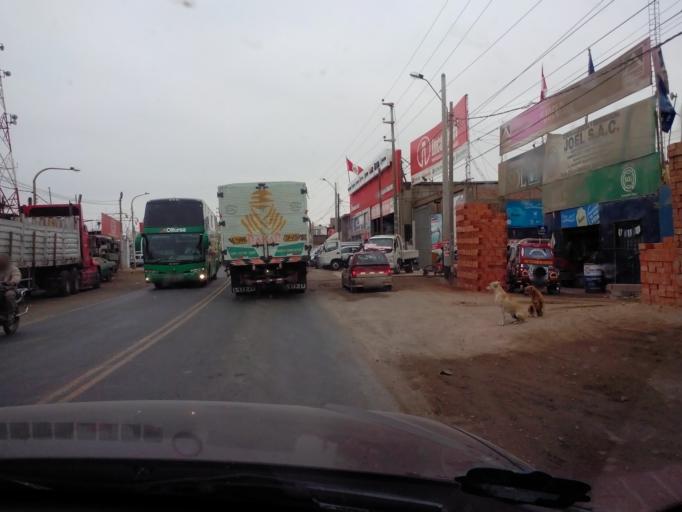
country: PE
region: Ica
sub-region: Provincia de Chincha
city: Chincha Alta
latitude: -13.4273
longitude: -76.1339
